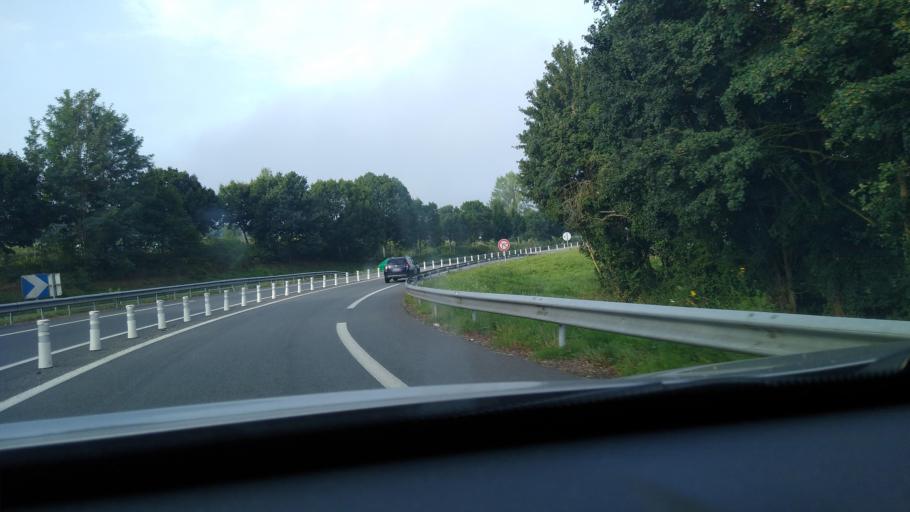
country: FR
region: Midi-Pyrenees
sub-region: Departement de la Haute-Garonne
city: Salies-du-Salat
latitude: 43.1275
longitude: 0.9429
